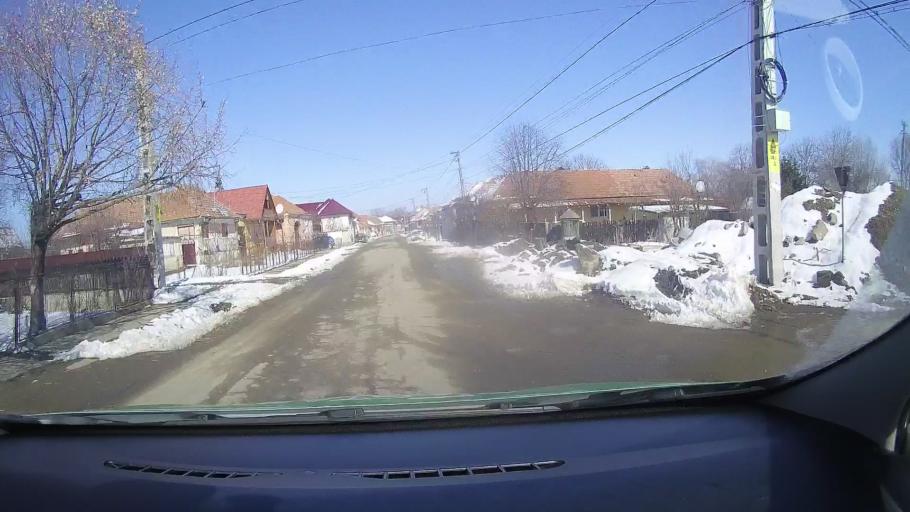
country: RO
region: Brasov
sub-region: Comuna Mandra
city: Mandra
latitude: 45.8207
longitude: 25.0055
